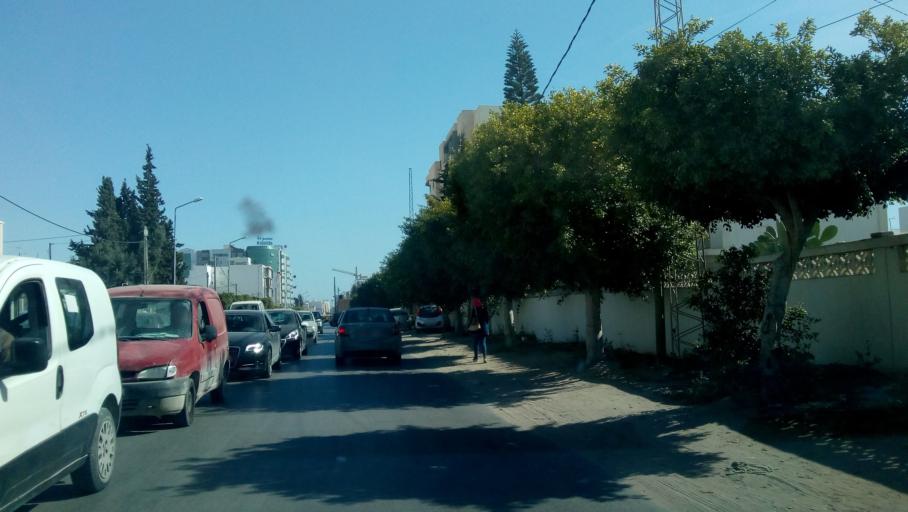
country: TN
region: Safaqis
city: Sfax
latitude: 34.7652
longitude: 10.7251
